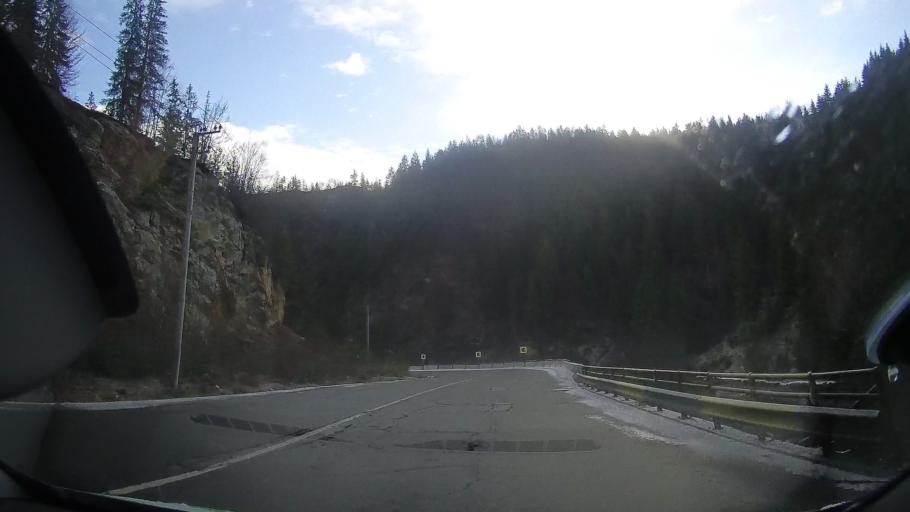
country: RO
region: Alba
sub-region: Comuna Albac
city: Albac
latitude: 46.4538
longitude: 22.9311
